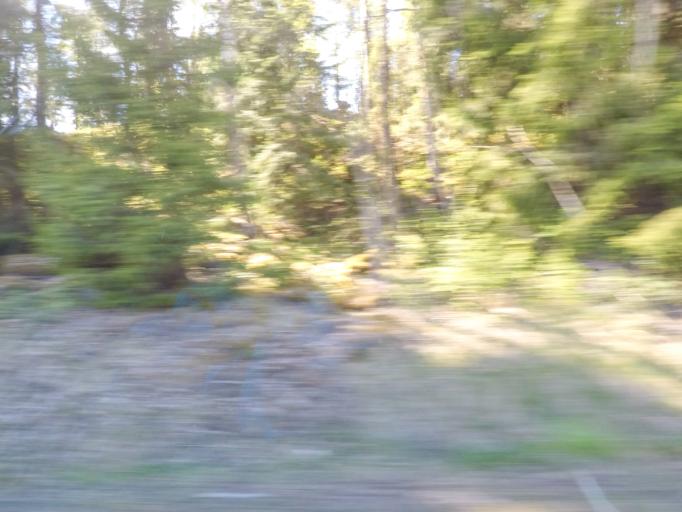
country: FI
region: Uusimaa
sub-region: Helsinki
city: Sammatti
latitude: 60.3489
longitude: 23.7996
